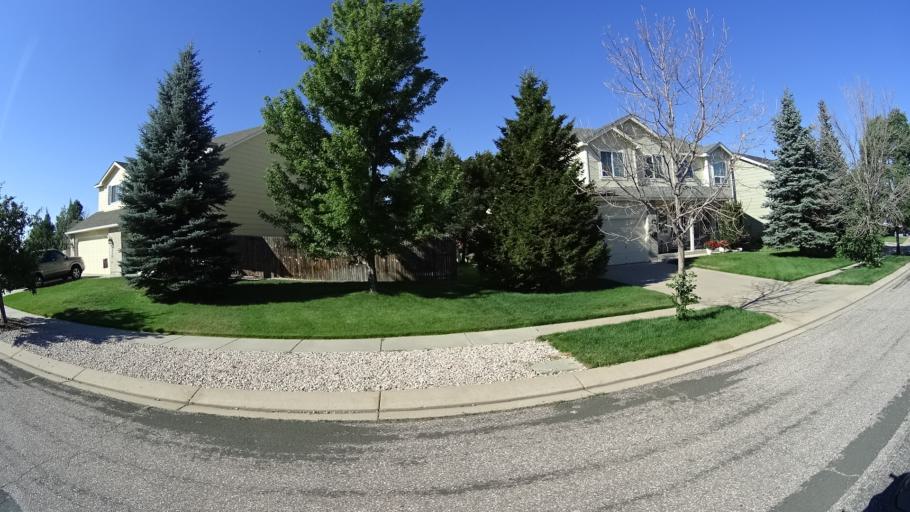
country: US
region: Colorado
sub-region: El Paso County
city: Black Forest
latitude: 38.9615
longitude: -104.7541
